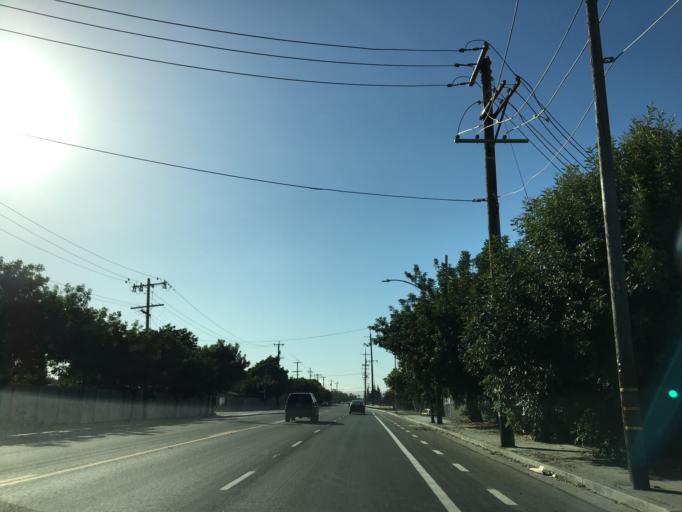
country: US
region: California
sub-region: Santa Clara County
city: Alum Rock
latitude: 37.3614
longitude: -121.8642
